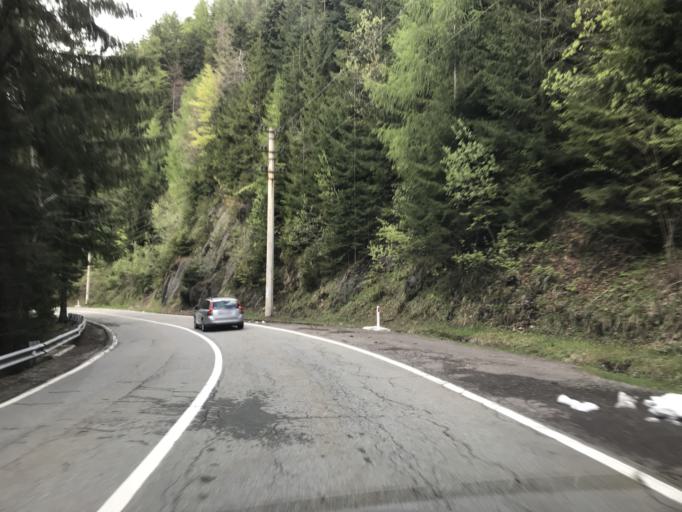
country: RO
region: Sibiu
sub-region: Comuna Cartisoara
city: Cartisoara
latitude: 45.6549
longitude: 24.6027
